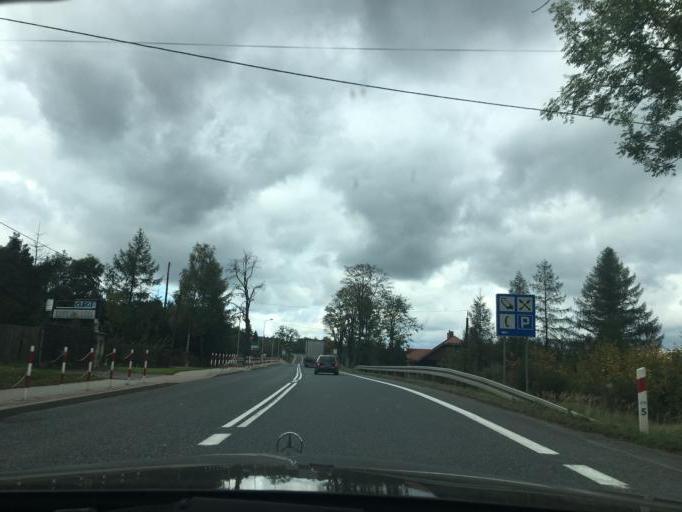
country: PL
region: Subcarpathian Voivodeship
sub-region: Powiat krosnienski
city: Dukla
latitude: 49.5423
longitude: 21.6914
